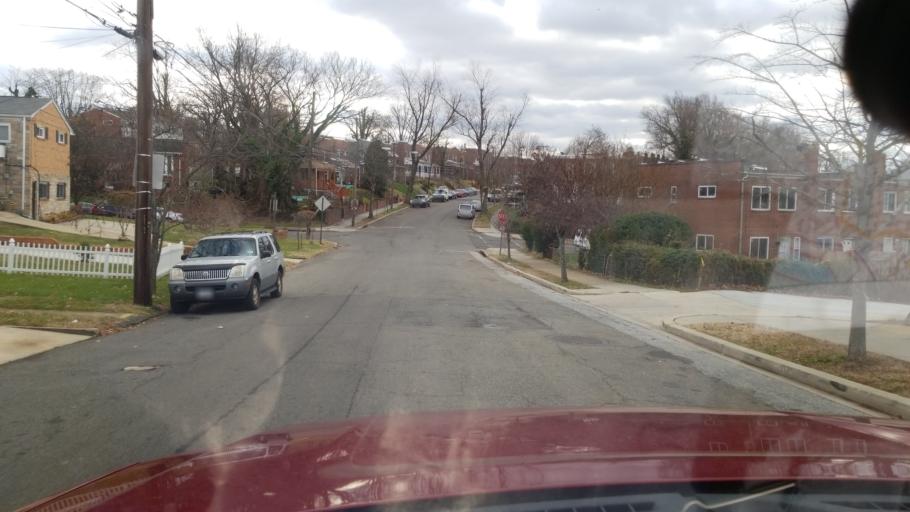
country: US
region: Maryland
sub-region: Prince George's County
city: Coral Hills
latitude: 38.8692
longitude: -76.9442
